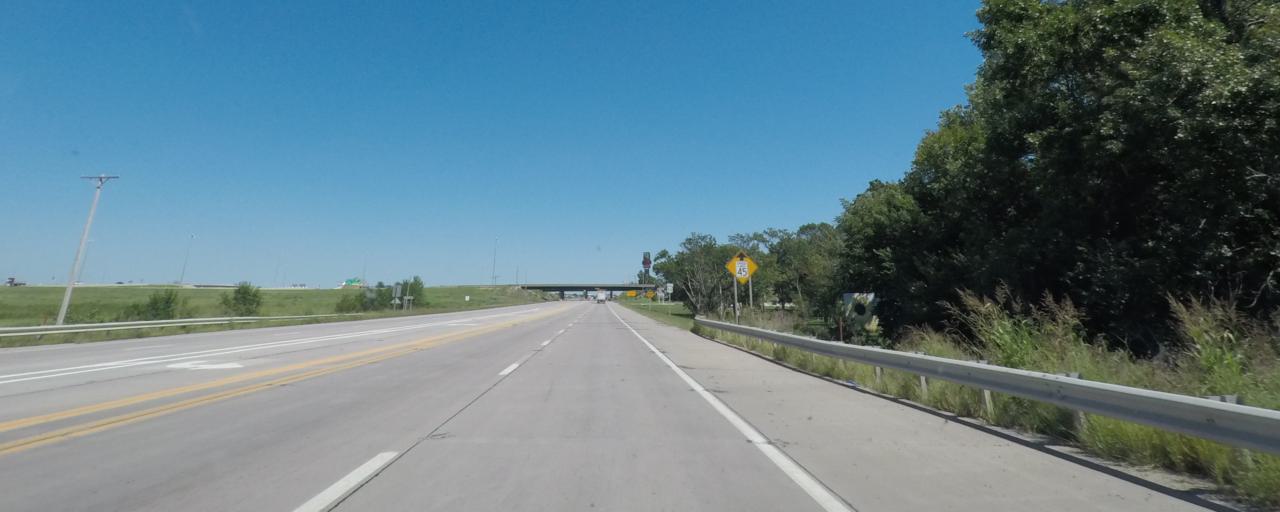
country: US
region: Kansas
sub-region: Lyon County
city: Emporia
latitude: 38.4122
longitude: -96.2440
